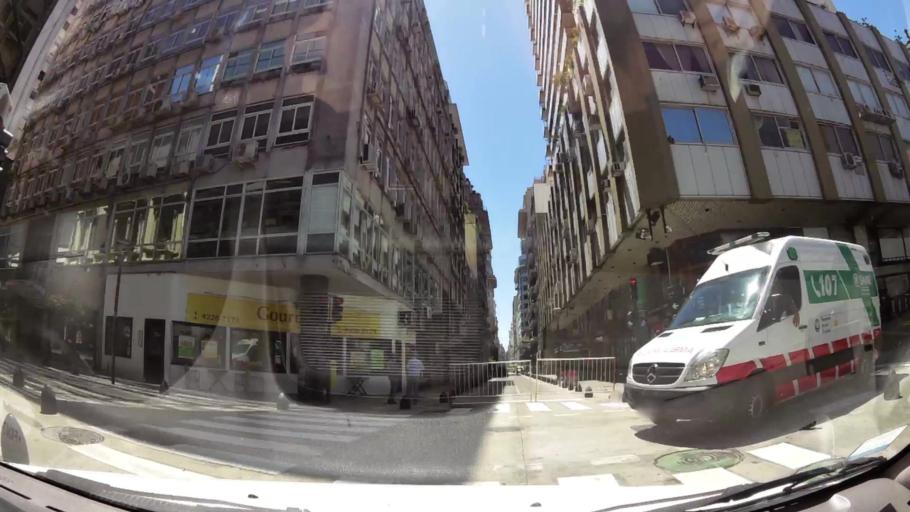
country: AR
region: Buenos Aires F.D.
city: Buenos Aires
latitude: -34.6062
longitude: -58.3795
